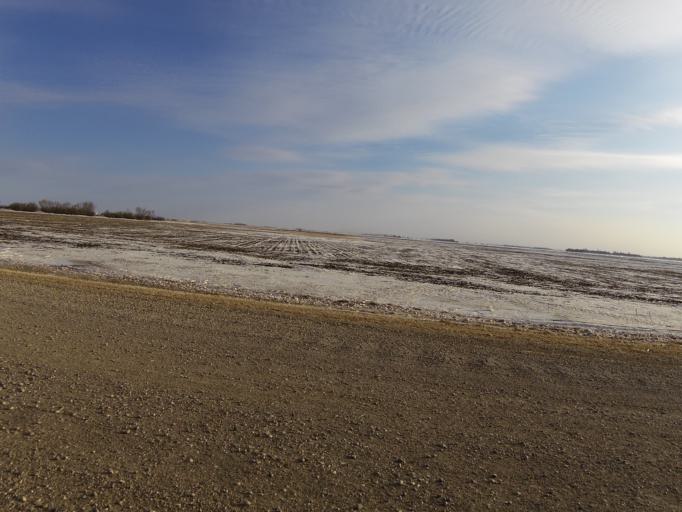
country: US
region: North Dakota
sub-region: Walsh County
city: Grafton
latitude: 48.4198
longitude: -97.3782
